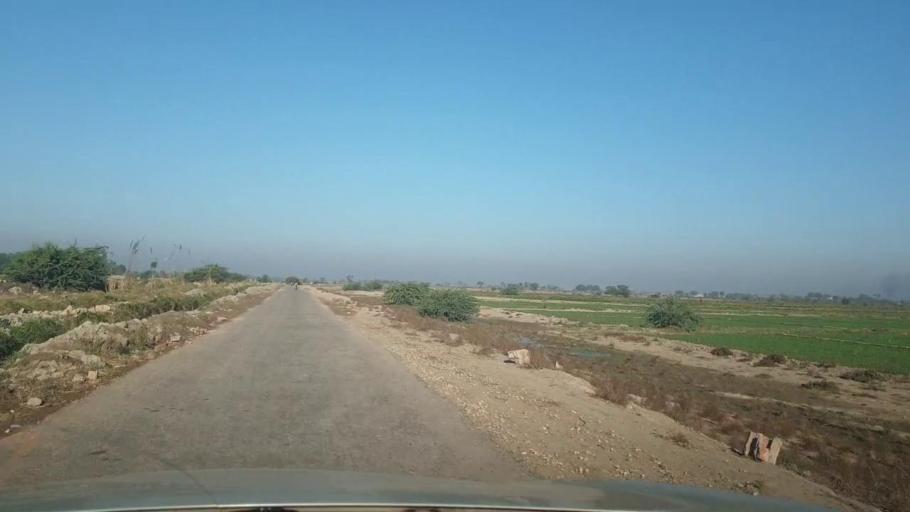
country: PK
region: Sindh
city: Bhan
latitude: 26.5512
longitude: 67.6983
